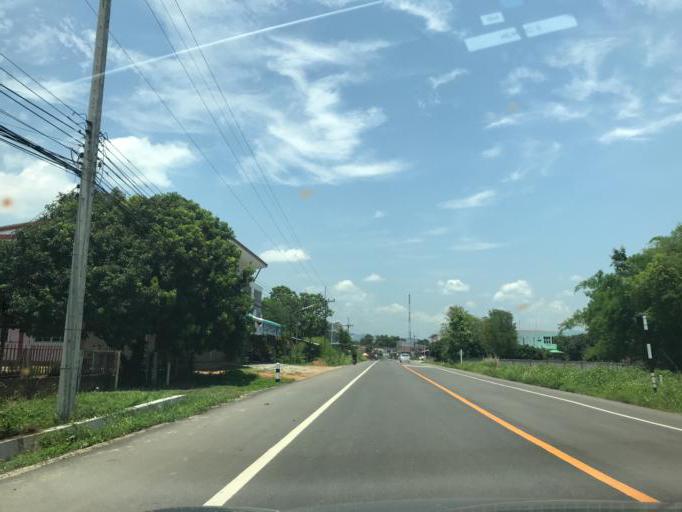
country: TH
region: Phayao
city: Phu Sang
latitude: 19.5942
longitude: 100.3175
